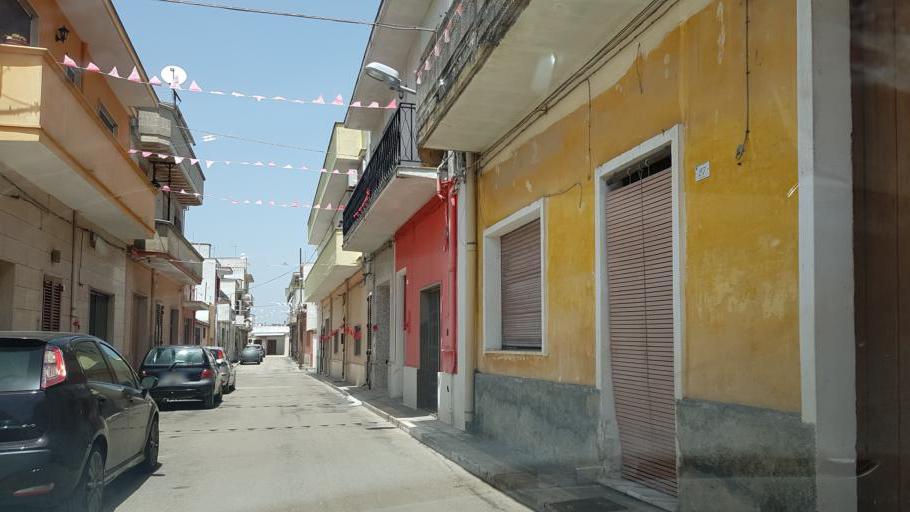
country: IT
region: Apulia
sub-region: Provincia di Brindisi
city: San Pancrazio Salentino
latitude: 40.4161
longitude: 17.8423
